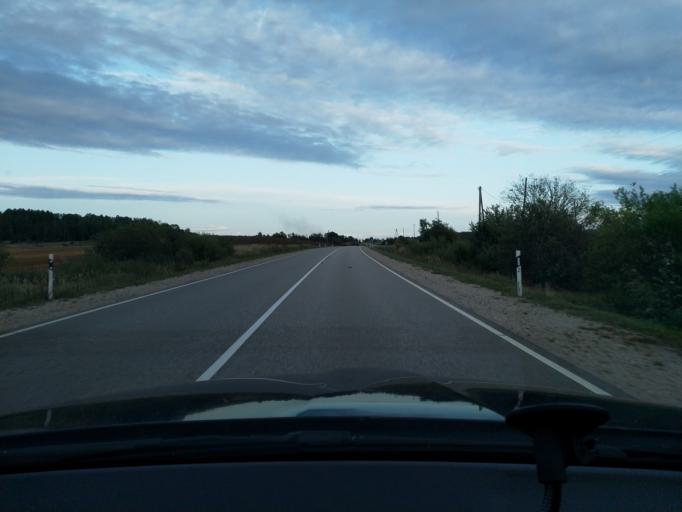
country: LV
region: Kandava
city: Kandava
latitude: 56.9304
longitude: 22.7488
